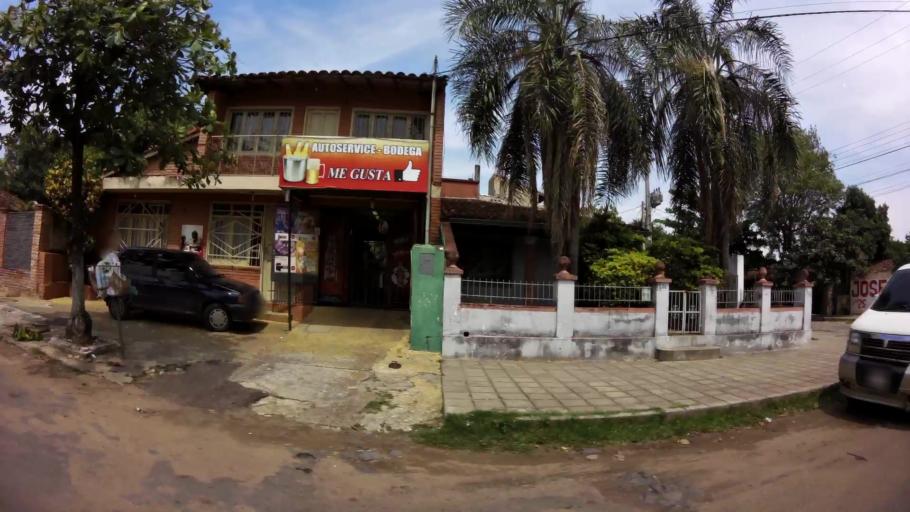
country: PY
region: Asuncion
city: Asuncion
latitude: -25.2695
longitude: -57.5878
